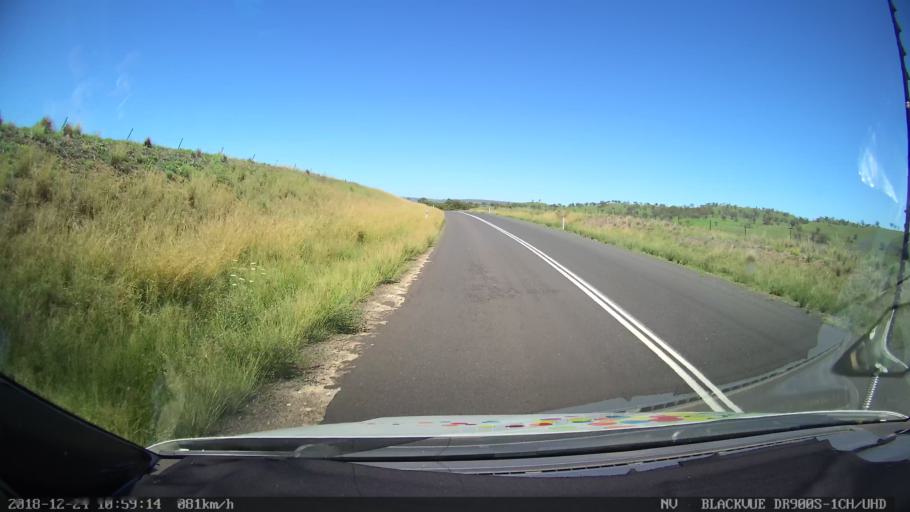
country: AU
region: New South Wales
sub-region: Upper Hunter Shire
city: Merriwa
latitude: -32.0541
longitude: 150.4024
